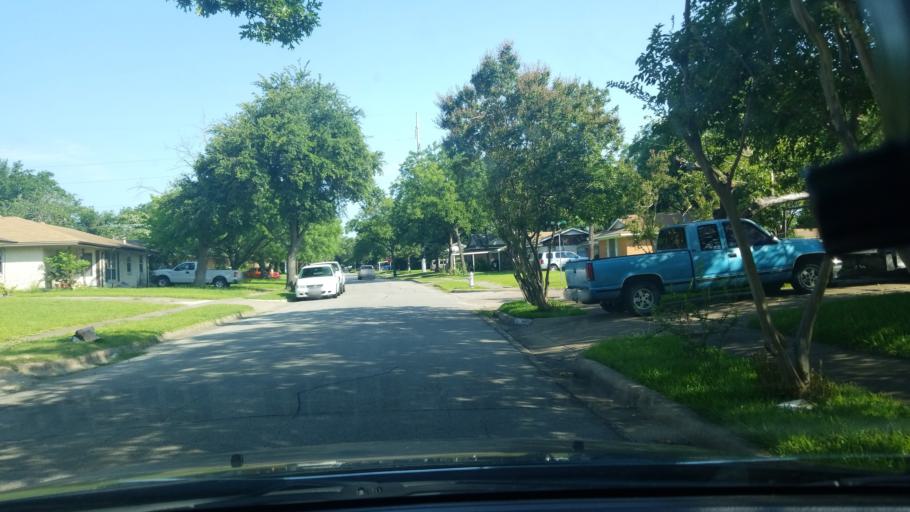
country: US
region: Texas
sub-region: Dallas County
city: Mesquite
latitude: 32.8250
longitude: -96.6390
